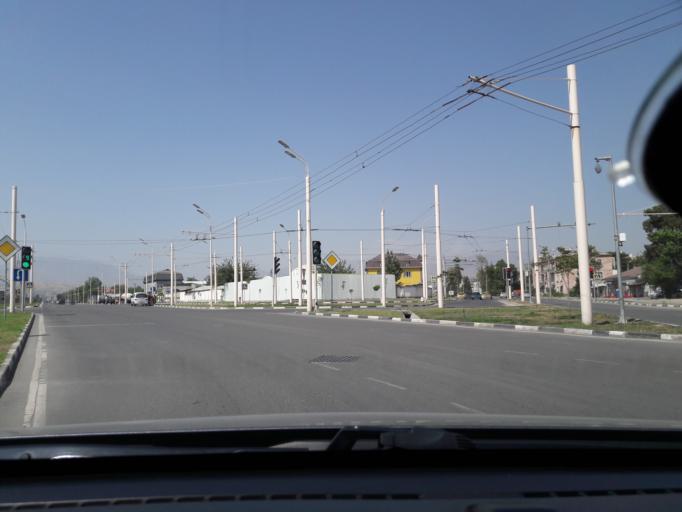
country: TJ
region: Dushanbe
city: Dushanbe
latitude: 38.5366
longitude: 68.7413
